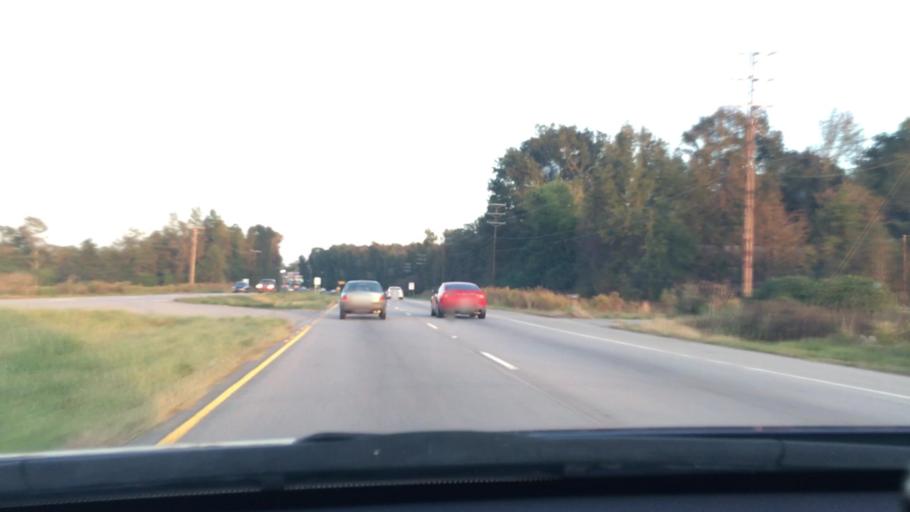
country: US
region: South Carolina
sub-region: Richland County
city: Hopkins
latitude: 33.9444
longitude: -80.8804
